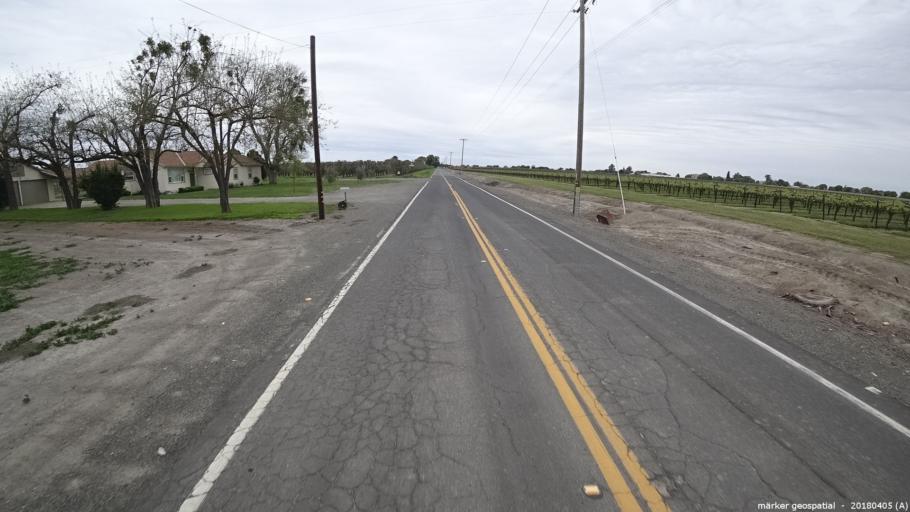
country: US
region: California
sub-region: Sacramento County
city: Walnut Grove
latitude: 38.3357
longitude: -121.5345
